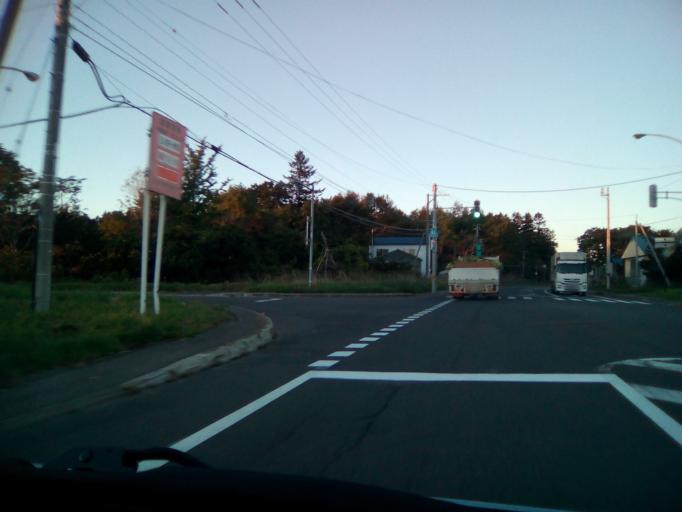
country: JP
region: Hokkaido
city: Niseko Town
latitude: 42.6941
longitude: 140.8391
